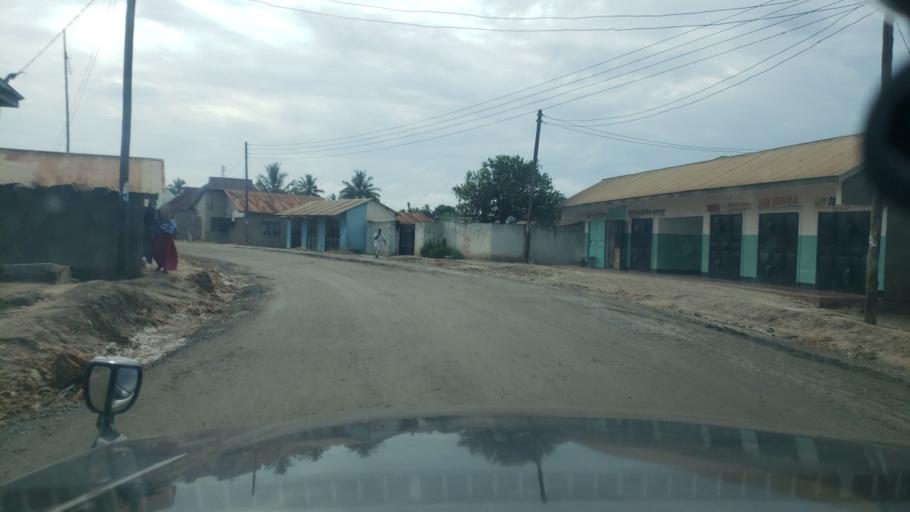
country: TZ
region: Pwani
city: Vikindu
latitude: -6.9273
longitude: 39.2535
